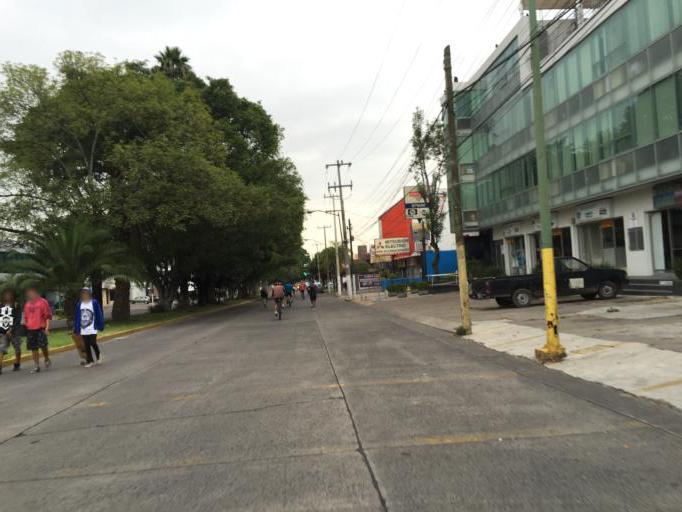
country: MX
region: Jalisco
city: Guadalajara
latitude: 20.6667
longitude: -103.3749
